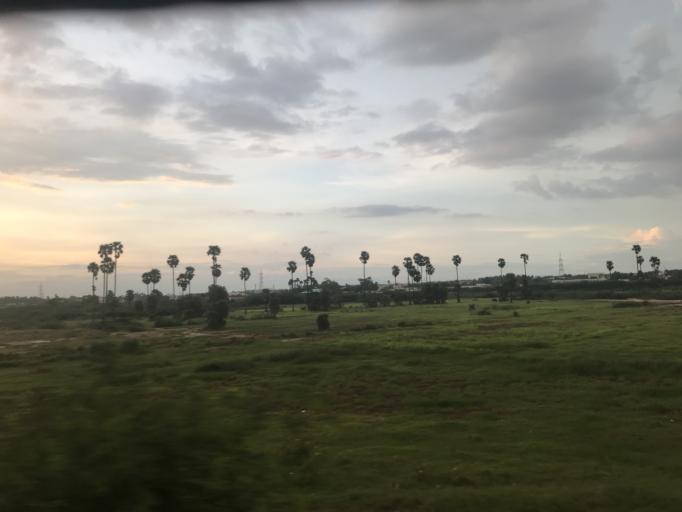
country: IN
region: Tamil Nadu
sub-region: Tiruppur
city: Tiruppur
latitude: 11.1333
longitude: 77.3729
